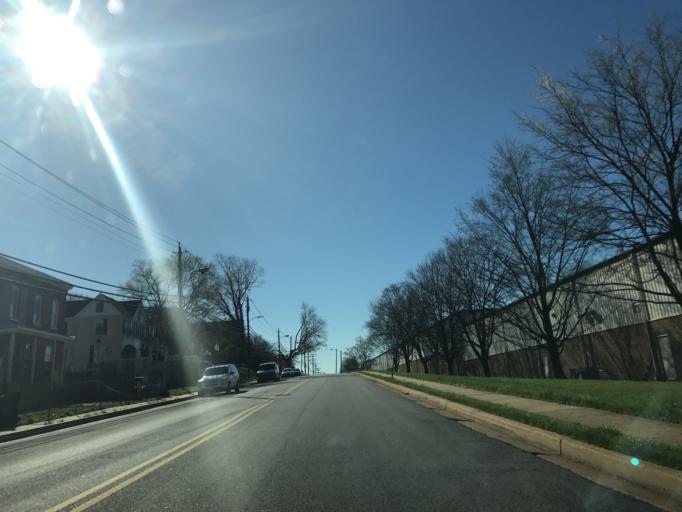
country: US
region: Maryland
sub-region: Baltimore County
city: Lansdowne
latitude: 39.2731
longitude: -76.6660
